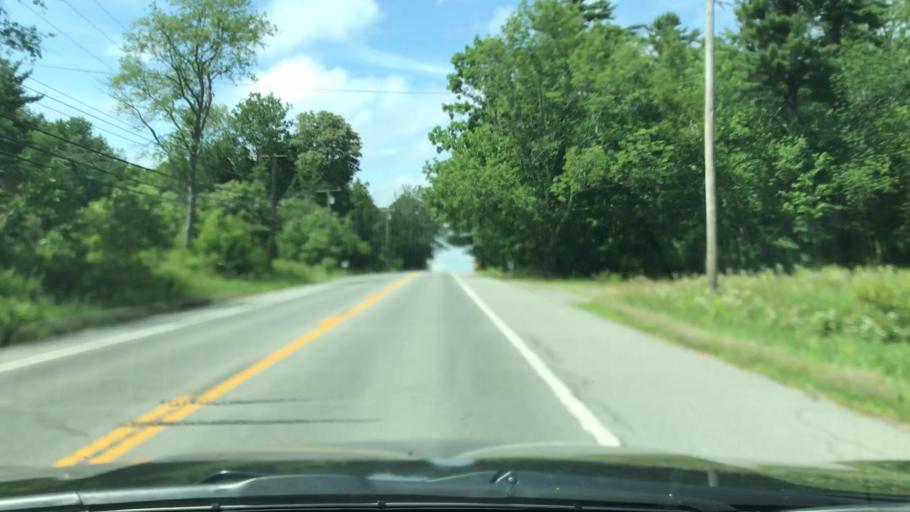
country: US
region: Maine
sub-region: Waldo County
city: Belfast
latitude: 44.3870
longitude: -68.9886
